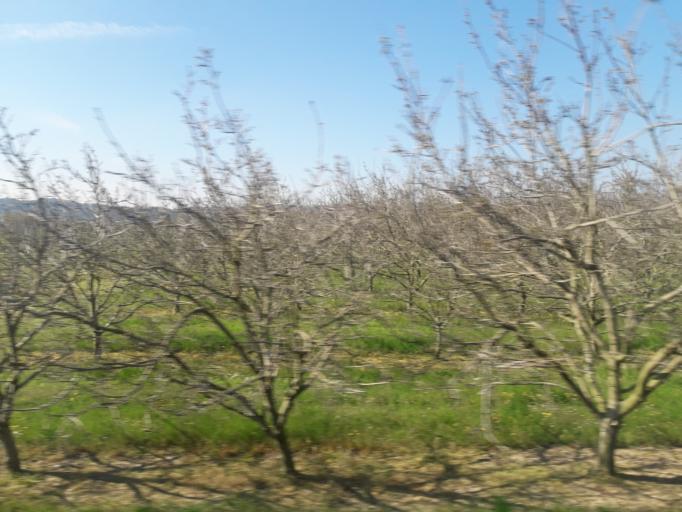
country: FR
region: Rhone-Alpes
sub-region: Departement de la Drome
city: Genissieux
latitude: 45.0612
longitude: 5.1047
